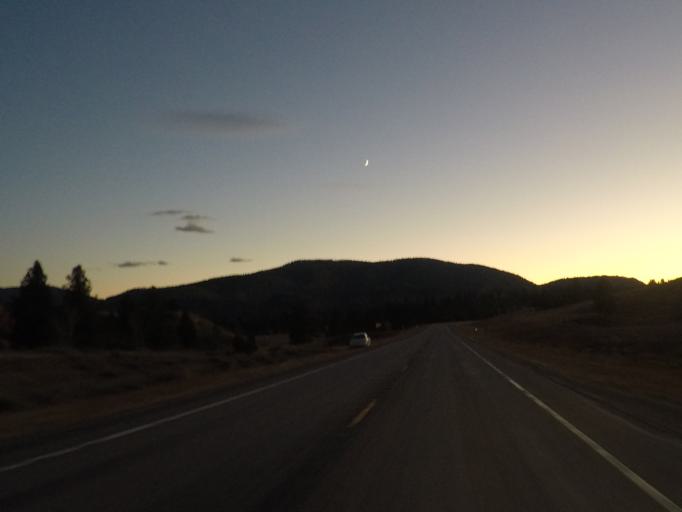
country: US
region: Montana
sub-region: Missoula County
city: Seeley Lake
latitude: 47.0324
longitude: -113.2352
